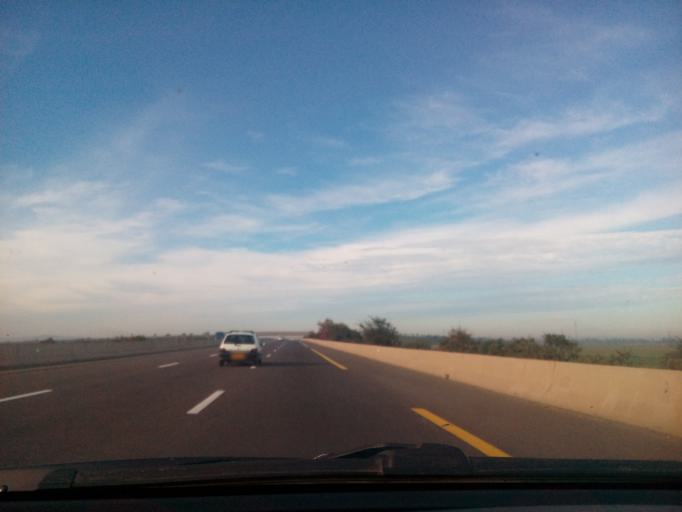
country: DZ
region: Mascara
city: Sig
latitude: 35.6165
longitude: 0.0108
